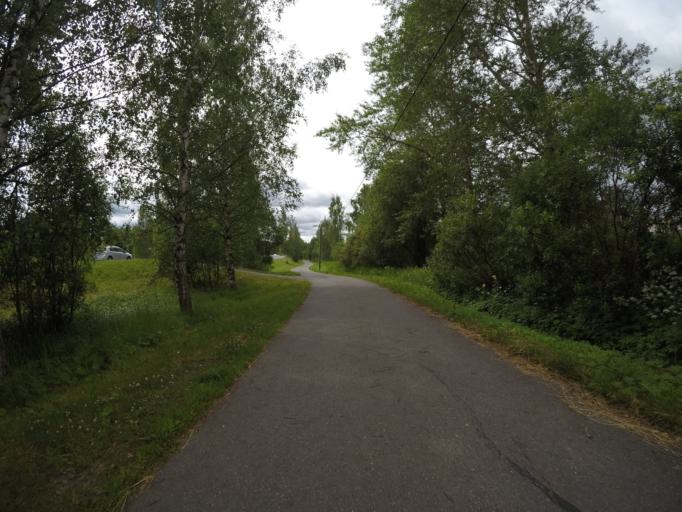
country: FI
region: Haeme
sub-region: Haemeenlinna
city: Haemeenlinna
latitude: 61.0020
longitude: 24.5022
